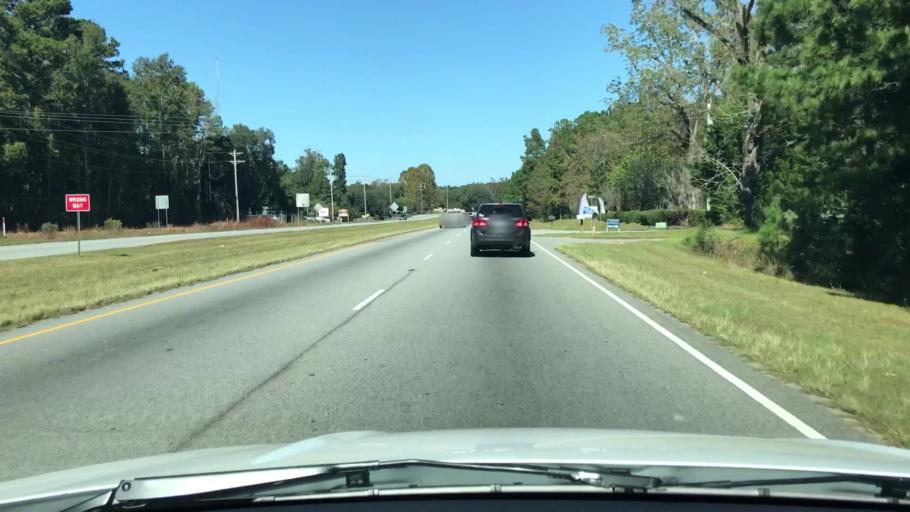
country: US
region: South Carolina
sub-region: Beaufort County
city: Bluffton
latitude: 32.3171
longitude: -80.9343
